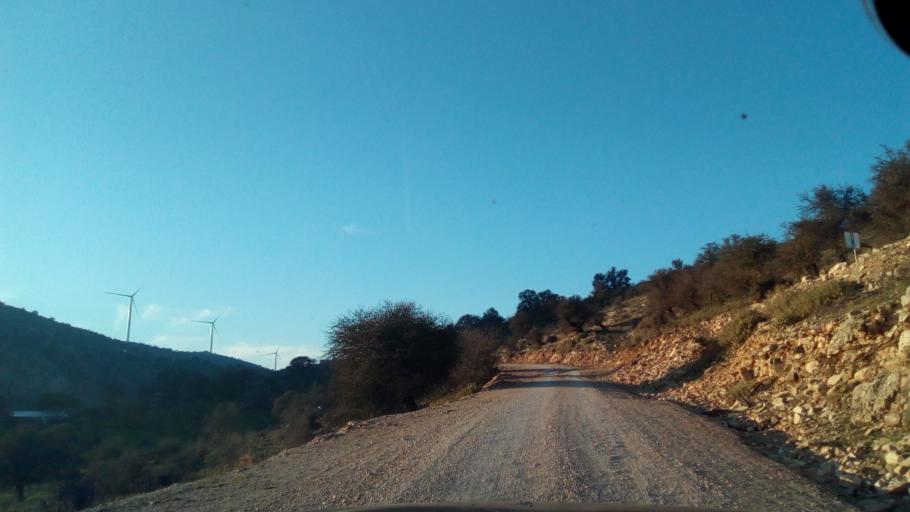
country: GR
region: West Greece
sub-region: Nomos Aitolias kai Akarnanias
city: Nafpaktos
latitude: 38.4565
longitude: 21.8427
